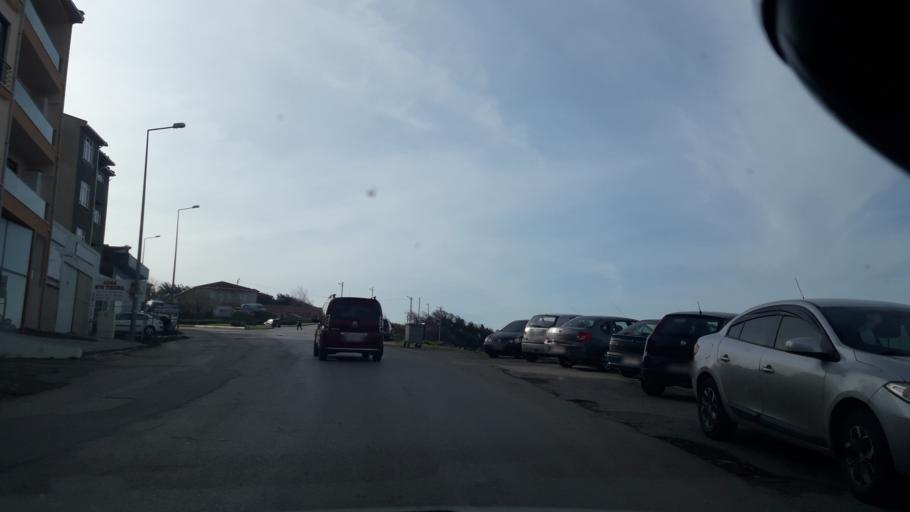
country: TR
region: Sinop
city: Sinop
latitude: 42.0253
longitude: 35.1397
